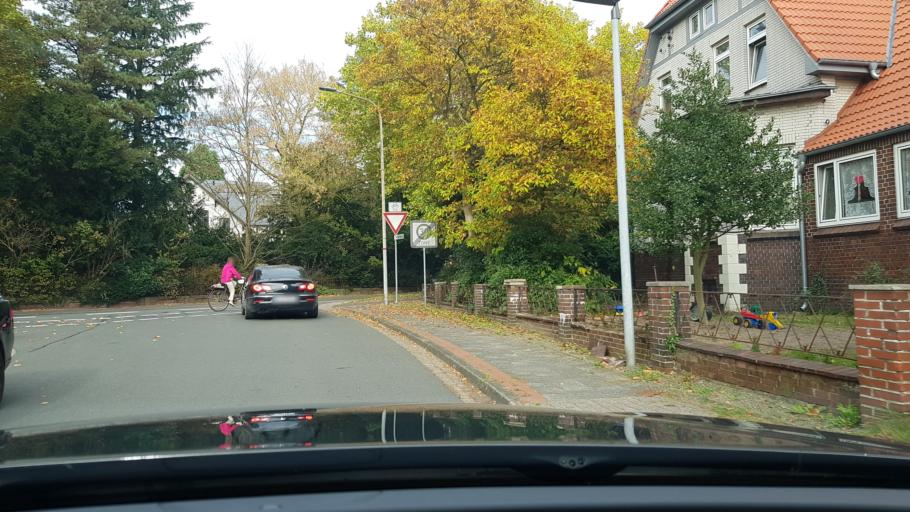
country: DE
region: Lower Saxony
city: Beverstedt
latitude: 53.4312
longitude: 8.8169
